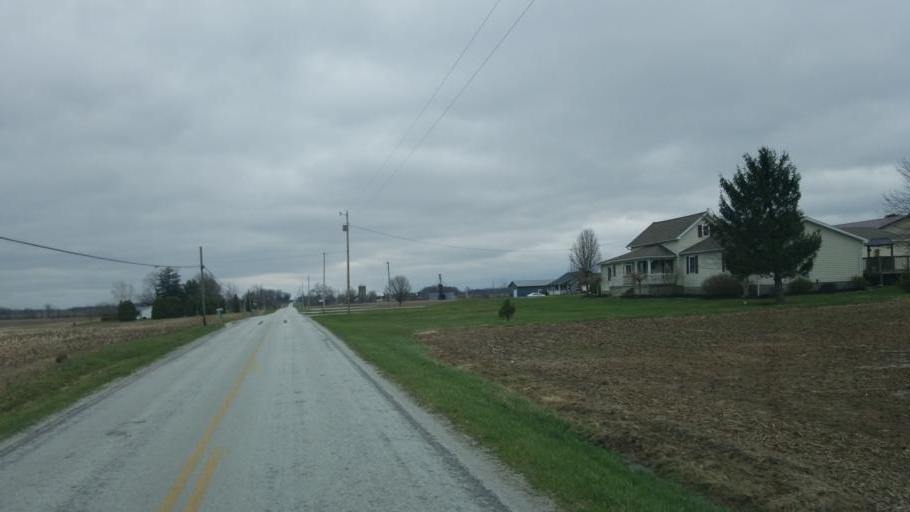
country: US
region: Ohio
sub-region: Hardin County
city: Kenton
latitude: 40.6587
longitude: -83.5630
